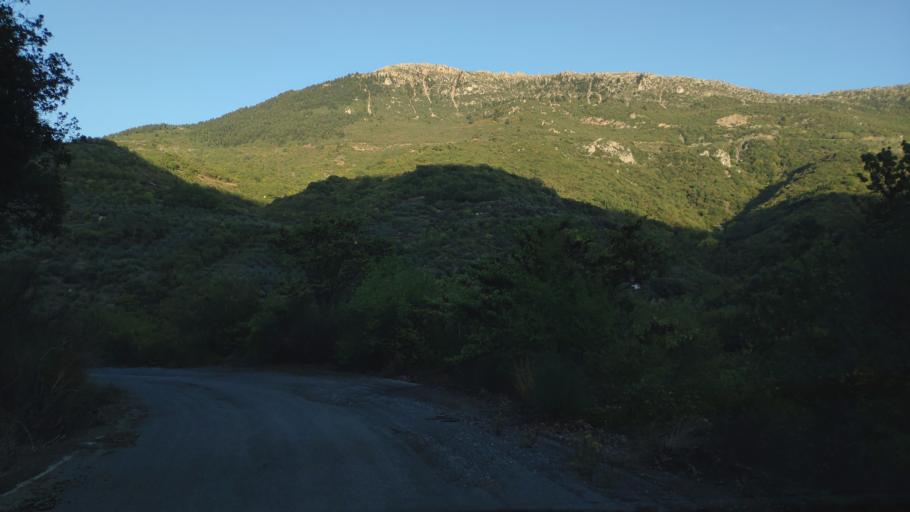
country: GR
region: Peloponnese
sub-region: Nomos Arkadias
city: Dimitsana
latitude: 37.5663
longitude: 22.0411
